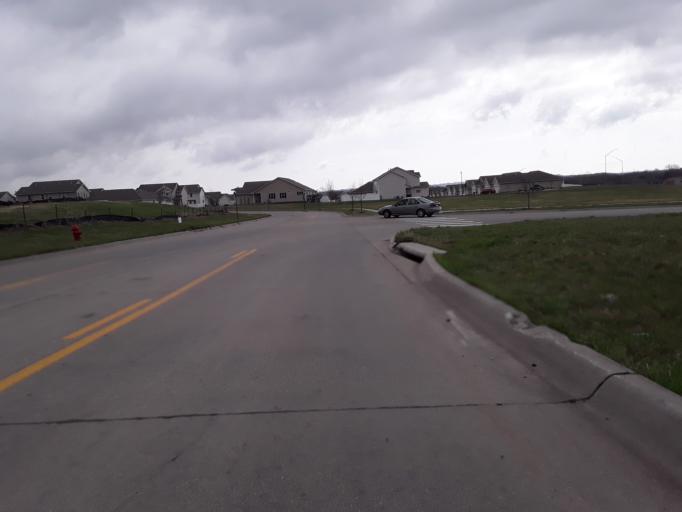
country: US
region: Nebraska
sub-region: Lancaster County
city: Lincoln
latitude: 40.8435
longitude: -96.6028
